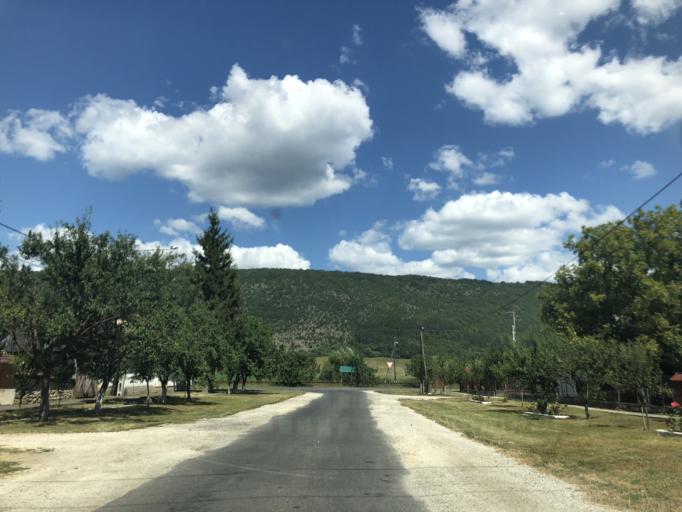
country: HU
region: Borsod-Abauj-Zemplen
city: Szendro
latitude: 48.5468
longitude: 20.7606
